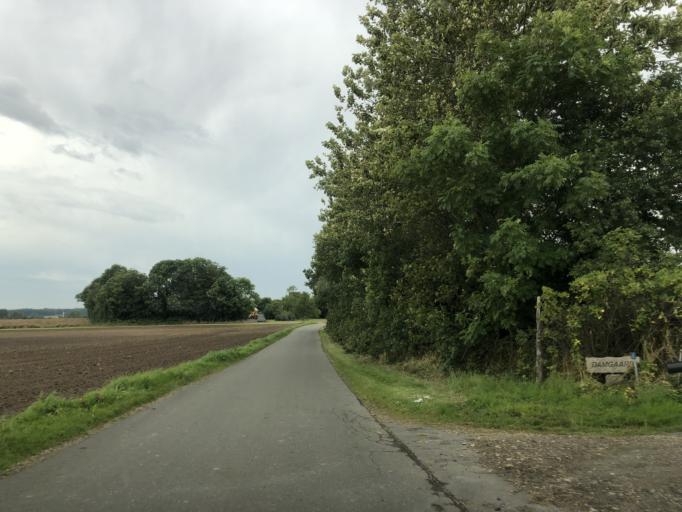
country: DK
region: Central Jutland
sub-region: Holstebro Kommune
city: Holstebro
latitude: 56.3951
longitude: 8.5962
